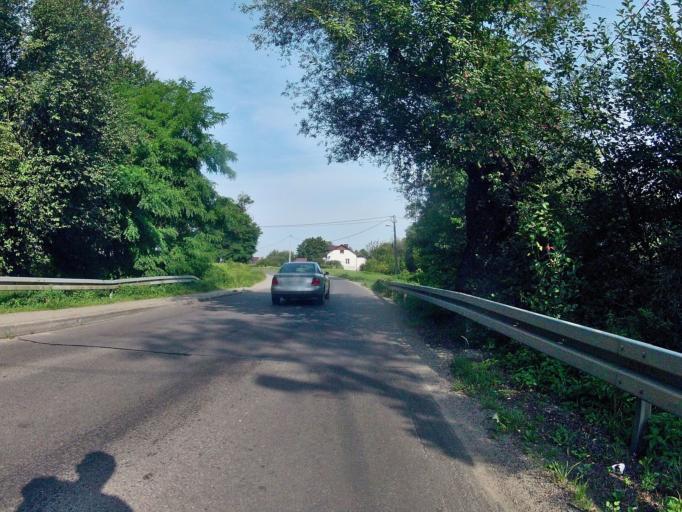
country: PL
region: Subcarpathian Voivodeship
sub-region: Powiat jasielski
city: Trzcinica
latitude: 49.7726
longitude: 21.4115
